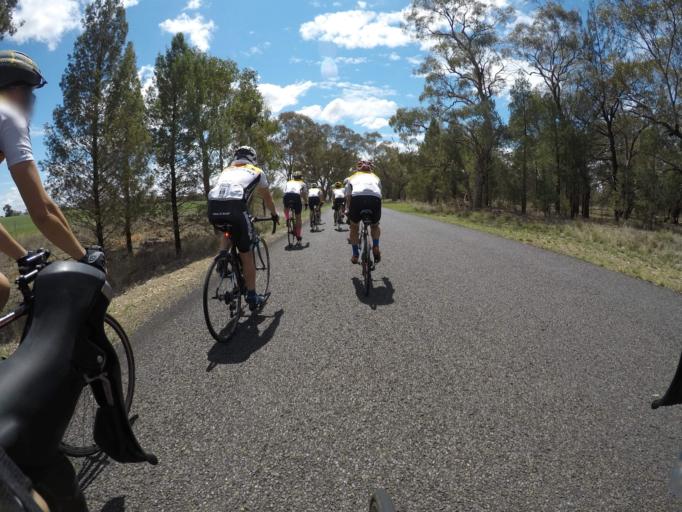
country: AU
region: New South Wales
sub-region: Dubbo Municipality
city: Dubbo
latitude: -32.3560
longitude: 148.5910
